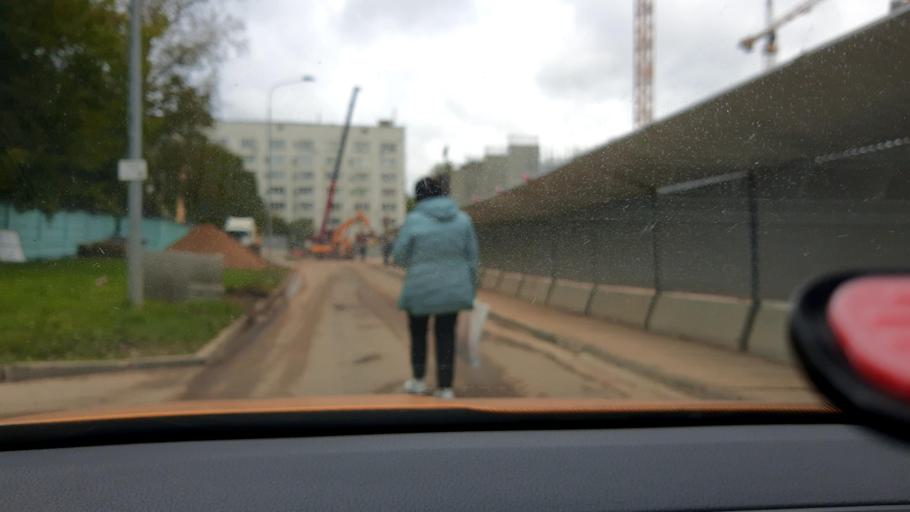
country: RU
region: Moscow
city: Pokrovskoye-Streshnevo
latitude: 55.8160
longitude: 37.4565
